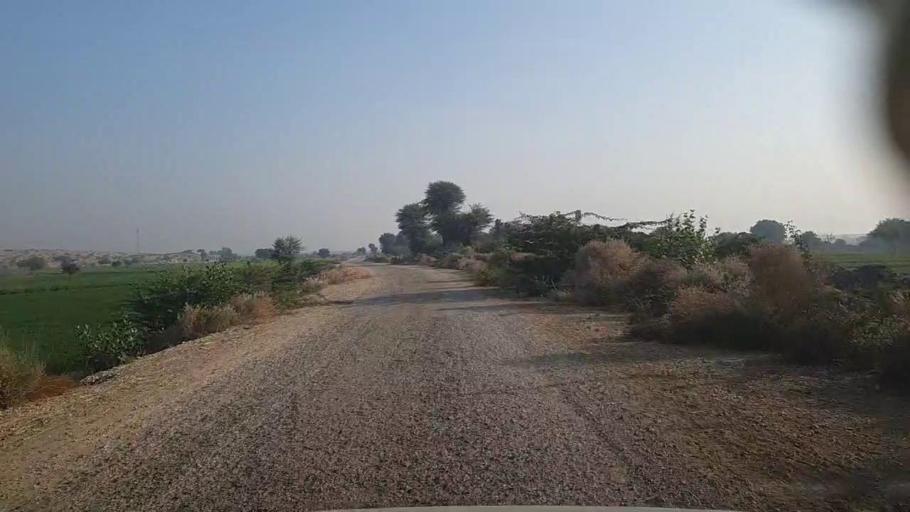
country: PK
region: Sindh
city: Karaundi
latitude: 26.7266
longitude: 68.4880
